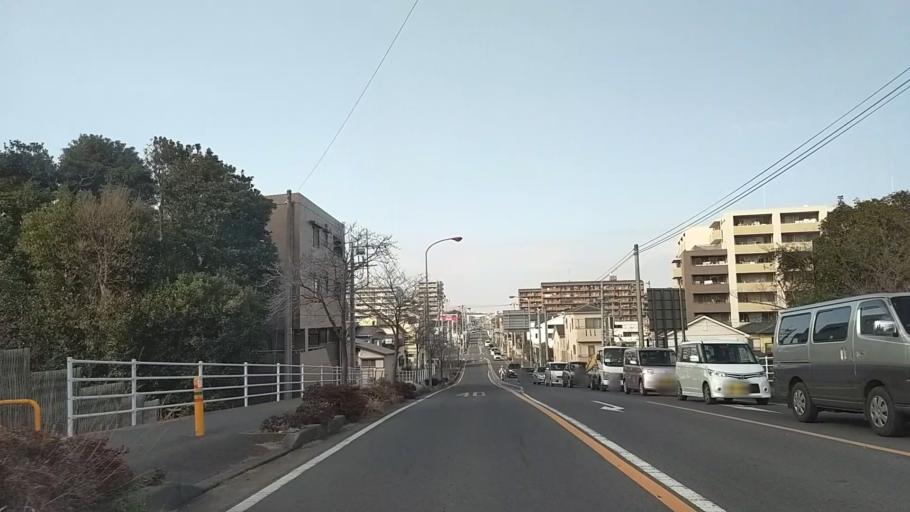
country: JP
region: Kanagawa
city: Chigasaki
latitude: 35.3367
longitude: 139.4142
